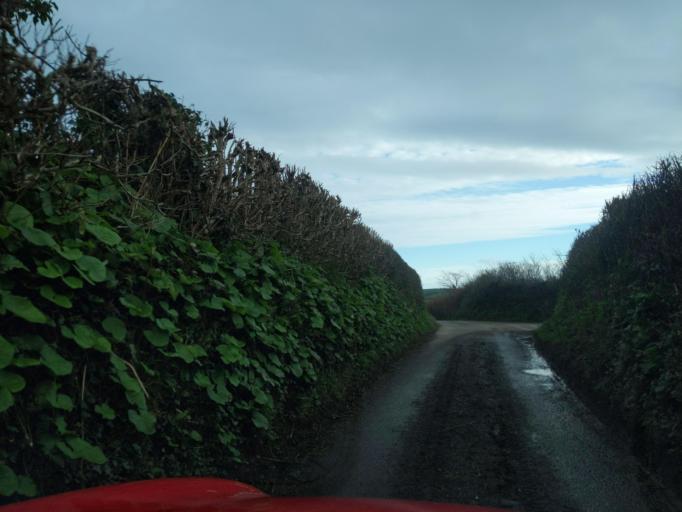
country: GB
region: England
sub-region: Devon
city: Salcombe
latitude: 50.2651
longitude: -3.6902
